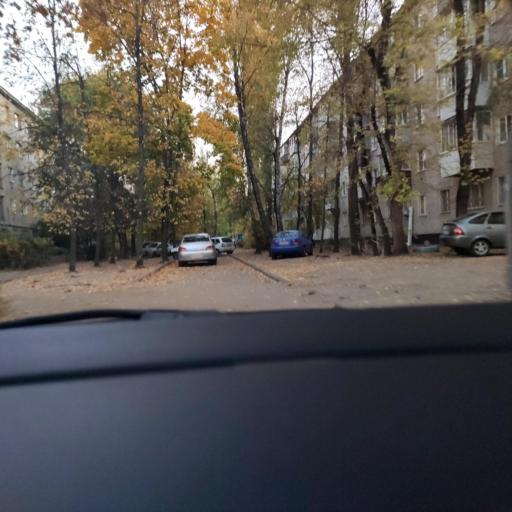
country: RU
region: Voronezj
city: Voronezh
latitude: 51.6521
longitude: 39.1554
